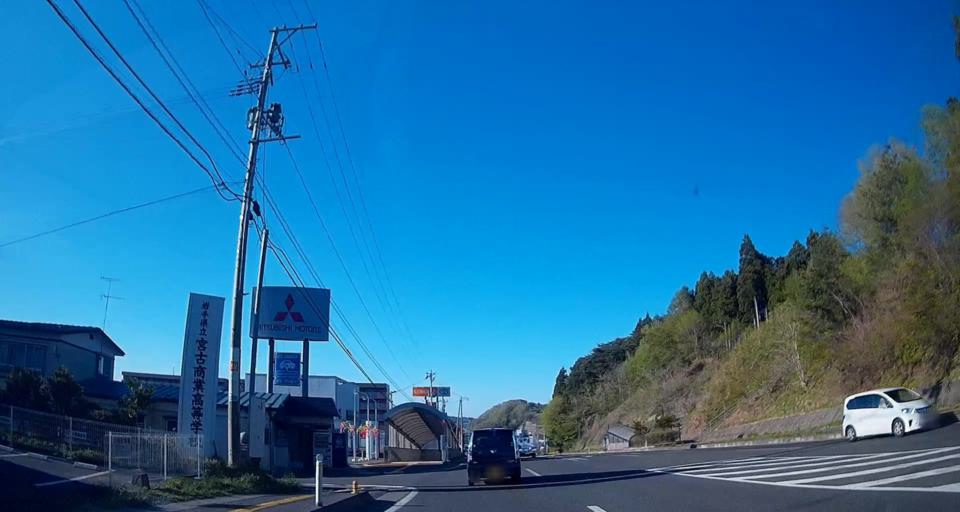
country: JP
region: Iwate
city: Miyako
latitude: 39.6175
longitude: 141.9611
